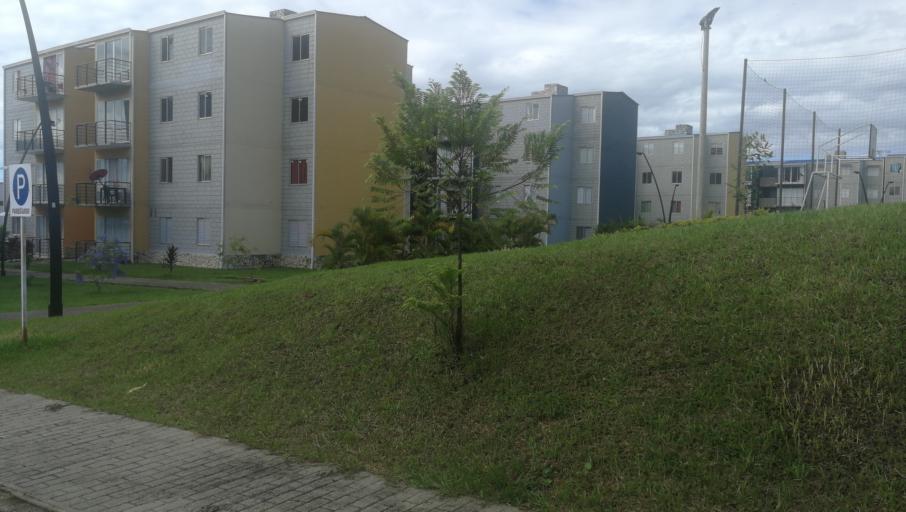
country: CO
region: Meta
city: Restrepo
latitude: 4.2512
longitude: -73.5688
